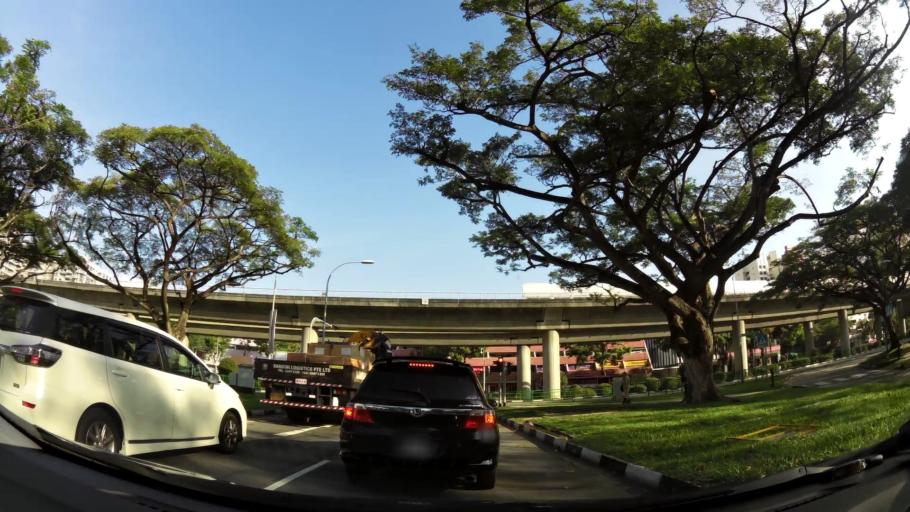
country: SG
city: Singapore
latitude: 1.3238
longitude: 103.9319
